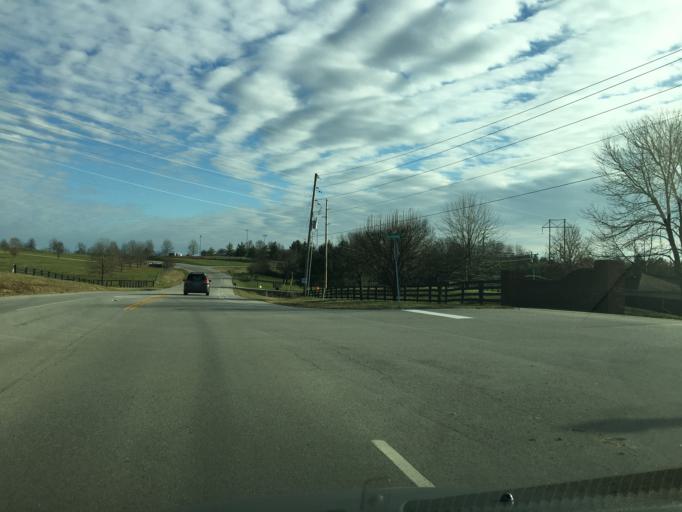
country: US
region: Kentucky
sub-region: Scott County
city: Georgetown
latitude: 38.2408
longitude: -84.5782
